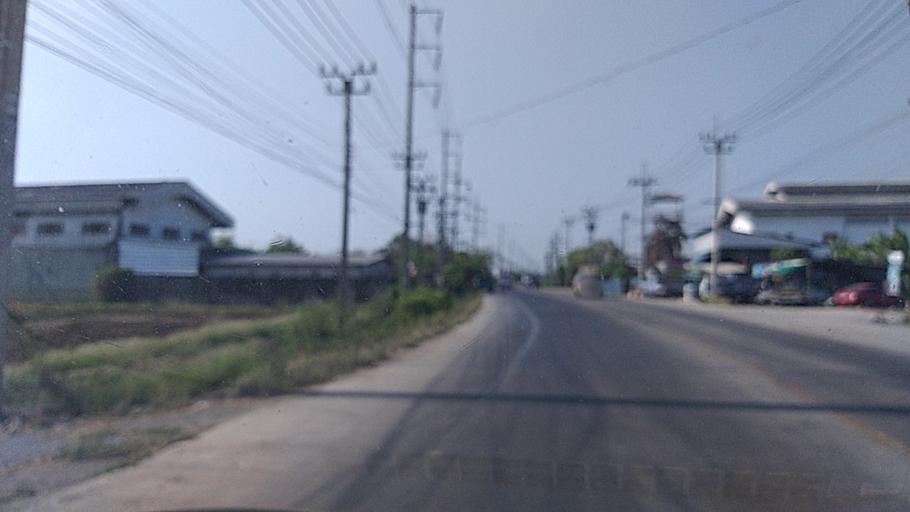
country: TH
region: Nonthaburi
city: Bang Yai
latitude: 13.8977
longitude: 100.3254
